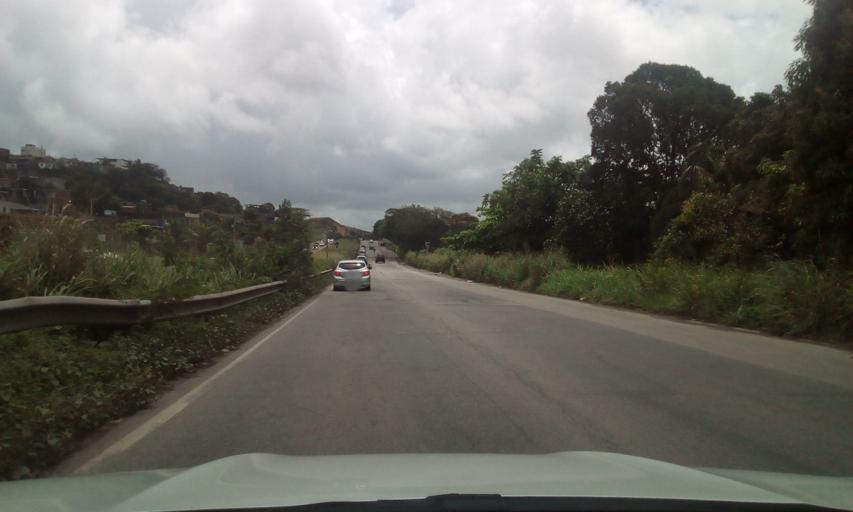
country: BR
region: Pernambuco
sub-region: Jaboatao Dos Guararapes
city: Jaboatao dos Guararapes
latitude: -8.1135
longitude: -34.9452
